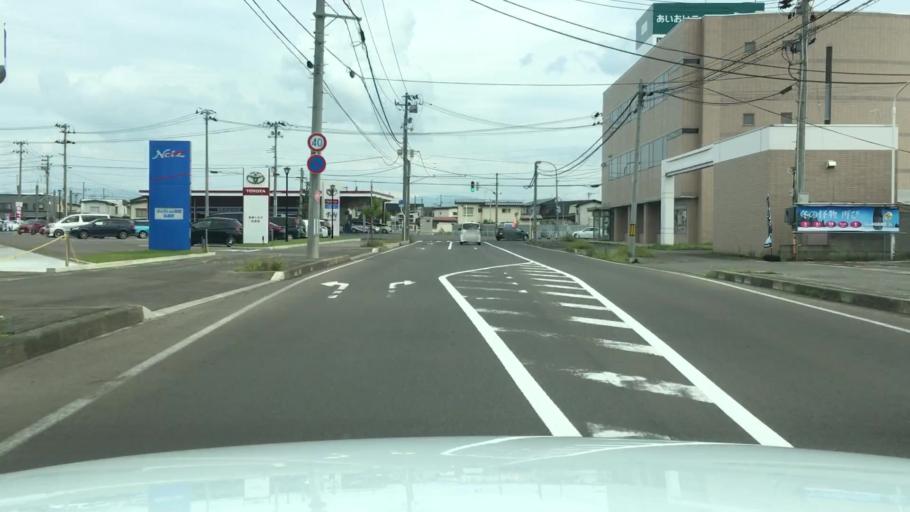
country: JP
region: Aomori
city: Hirosaki
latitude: 40.6150
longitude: 140.4896
